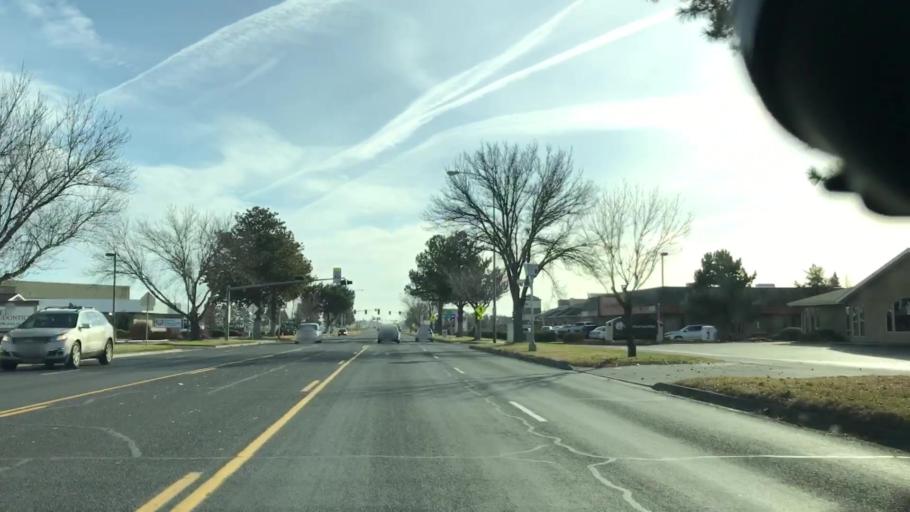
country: US
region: Washington
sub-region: Grant County
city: Moses Lake
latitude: 47.1150
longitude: -119.2625
